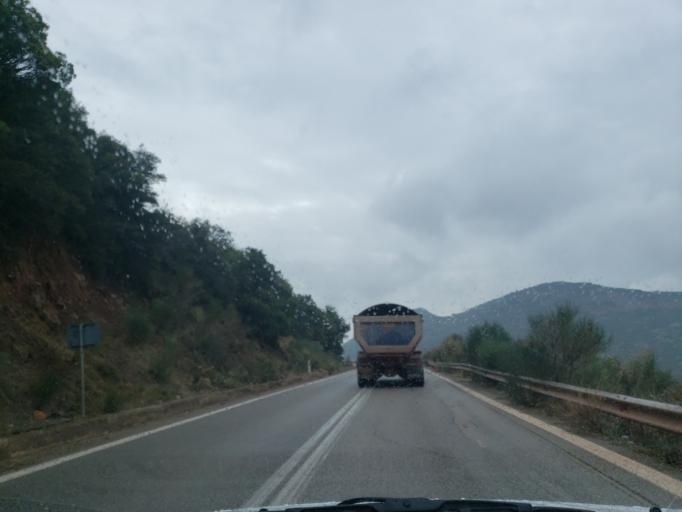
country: GR
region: Central Greece
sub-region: Nomos Fokidos
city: Amfissa
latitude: 38.5800
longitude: 22.3928
